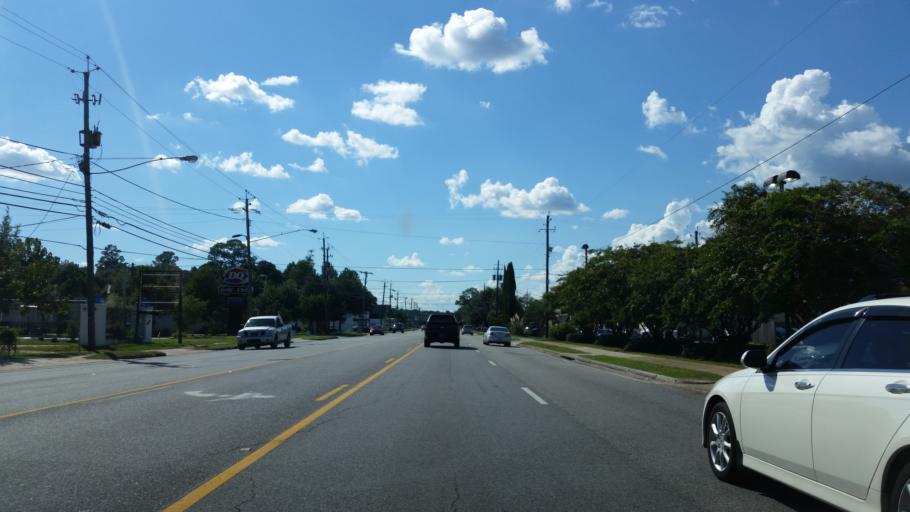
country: US
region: Alabama
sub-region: Mobile County
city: Prichard
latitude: 30.7015
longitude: -88.1160
